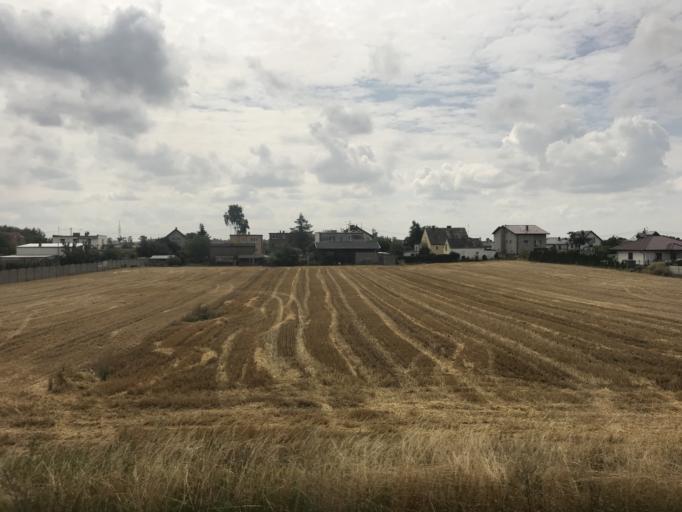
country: PL
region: Greater Poland Voivodeship
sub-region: Powiat gnieznienski
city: Gniezno
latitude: 52.5218
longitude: 17.5620
